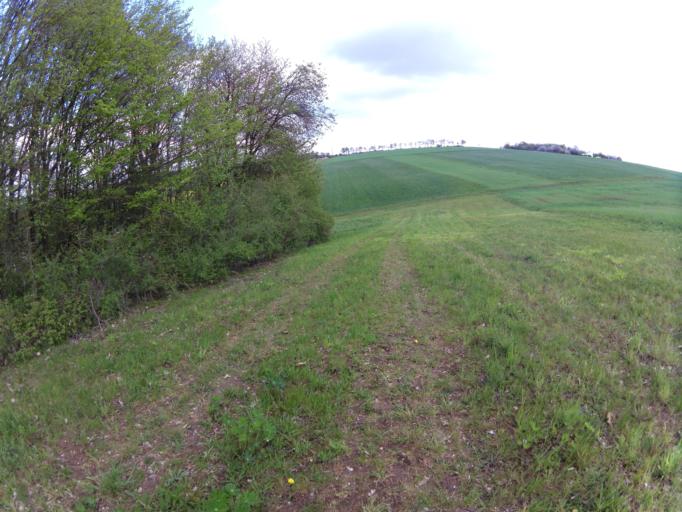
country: DE
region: Bavaria
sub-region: Regierungsbezirk Unterfranken
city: Hettstadt
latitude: 49.7943
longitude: 9.7911
